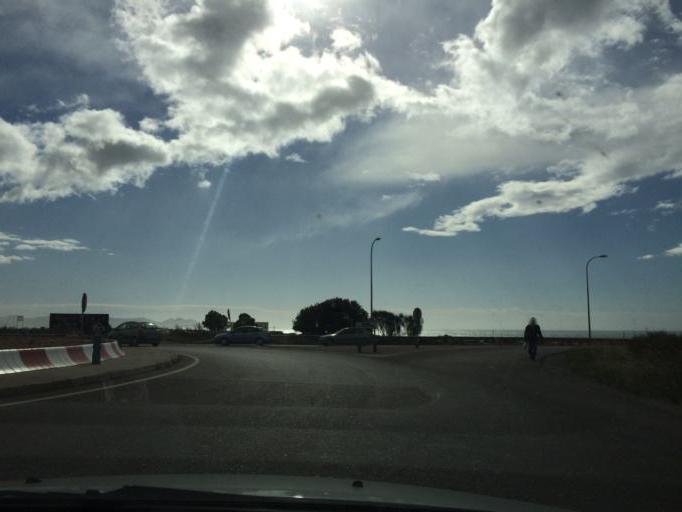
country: ES
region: Andalusia
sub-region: Provincia de Almeria
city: Retamar
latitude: 36.8550
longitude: -2.3453
